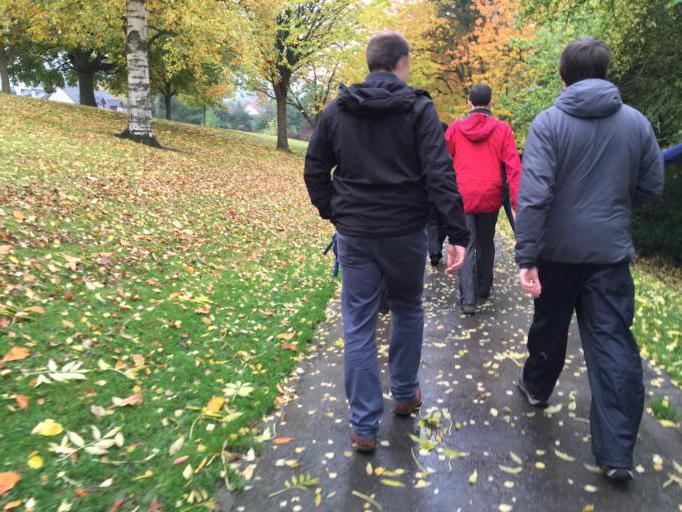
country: GB
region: Scotland
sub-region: Perth and Kinross
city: Perth
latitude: 56.3923
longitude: -3.4219
